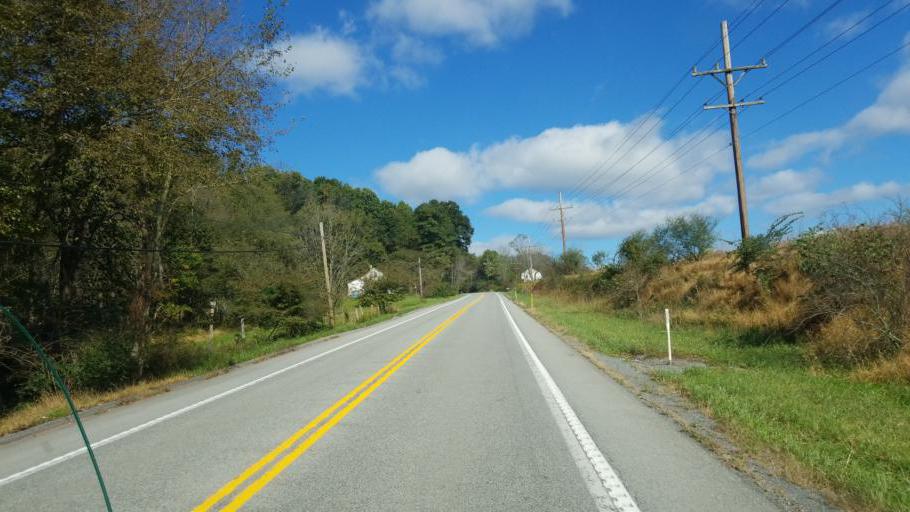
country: US
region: Pennsylvania
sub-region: Fulton County
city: McConnellsburg
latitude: 39.9567
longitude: -78.0246
